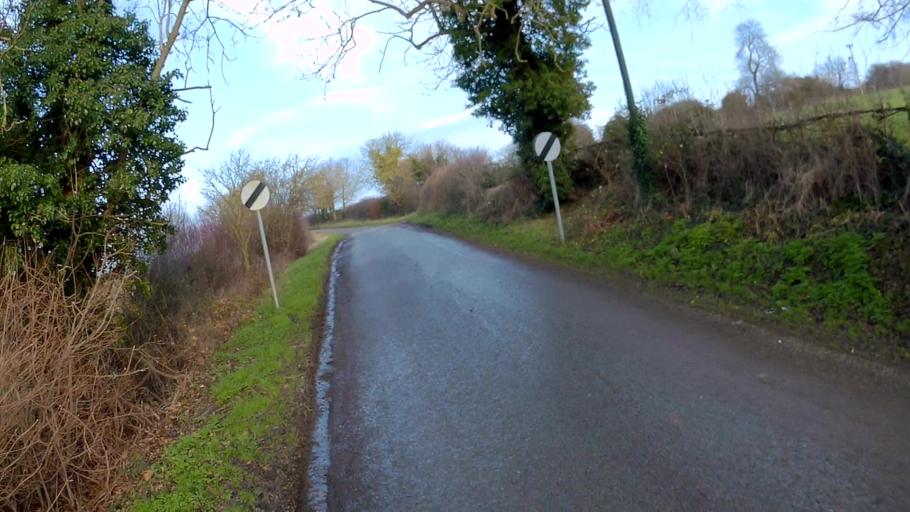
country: GB
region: England
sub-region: Lincolnshire
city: Bourne
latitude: 52.7437
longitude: -0.4190
